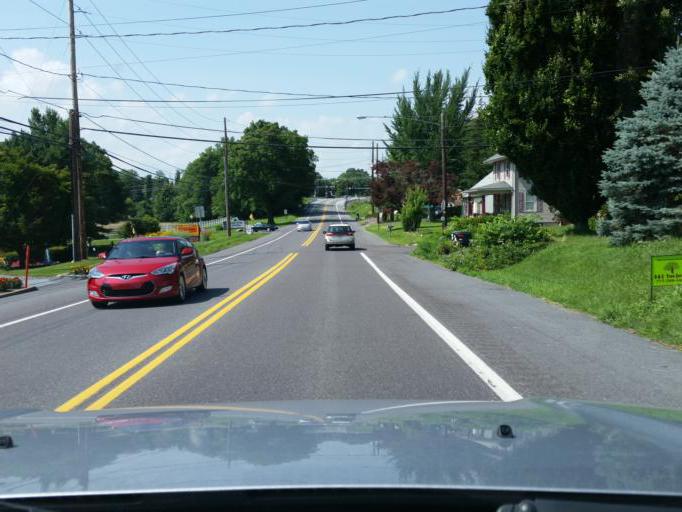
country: US
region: Pennsylvania
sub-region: Dauphin County
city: Hummelstown
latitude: 40.2546
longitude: -76.7089
